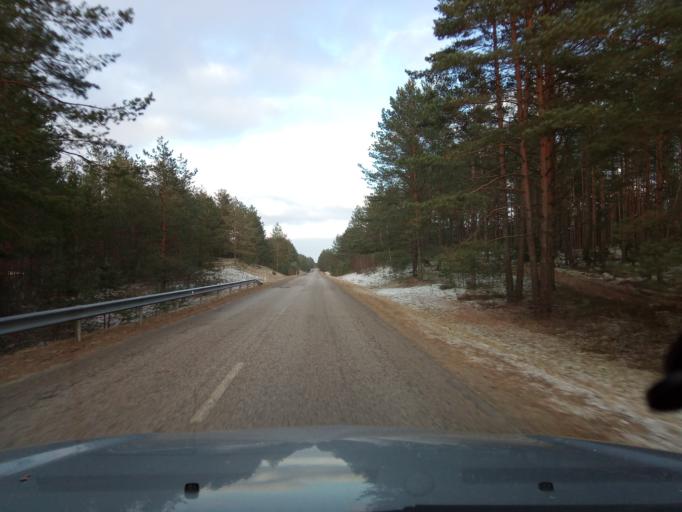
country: LT
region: Alytaus apskritis
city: Varena
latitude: 54.1100
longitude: 24.4388
